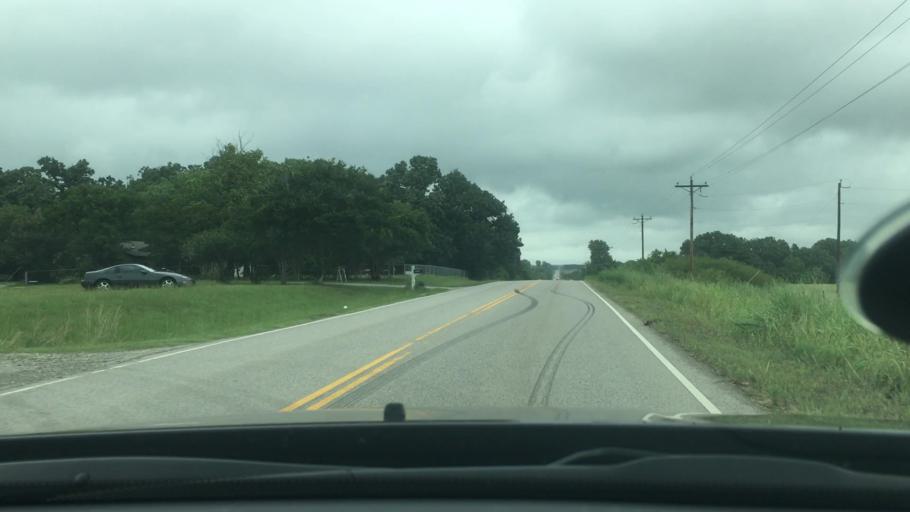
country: US
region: Oklahoma
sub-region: Bryan County
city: Calera
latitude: 33.9498
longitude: -96.5004
